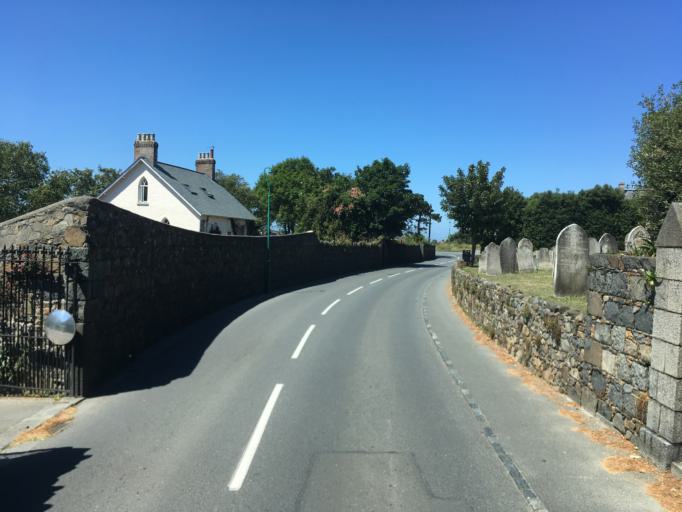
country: GG
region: St Peter Port
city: Saint Peter Port
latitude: 49.4924
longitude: -2.5396
